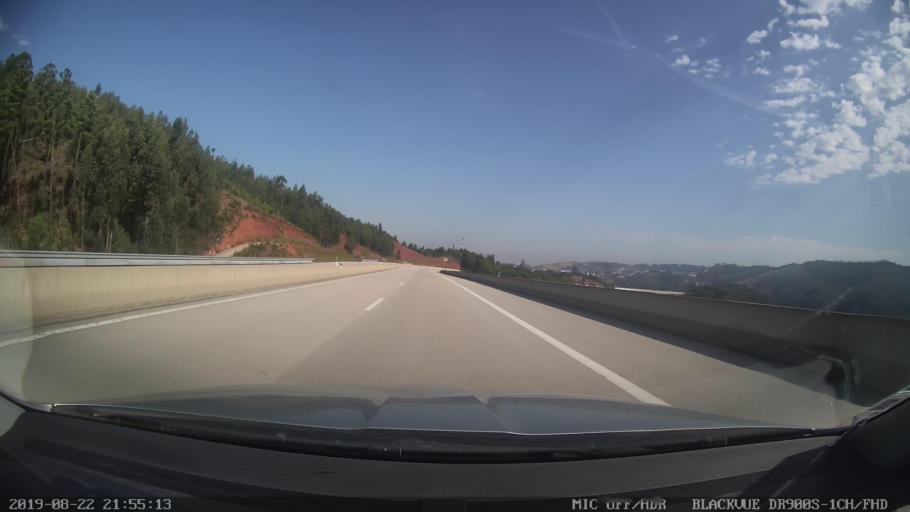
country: PT
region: Coimbra
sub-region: Coimbra
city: Coimbra
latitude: 40.1498
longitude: -8.3839
